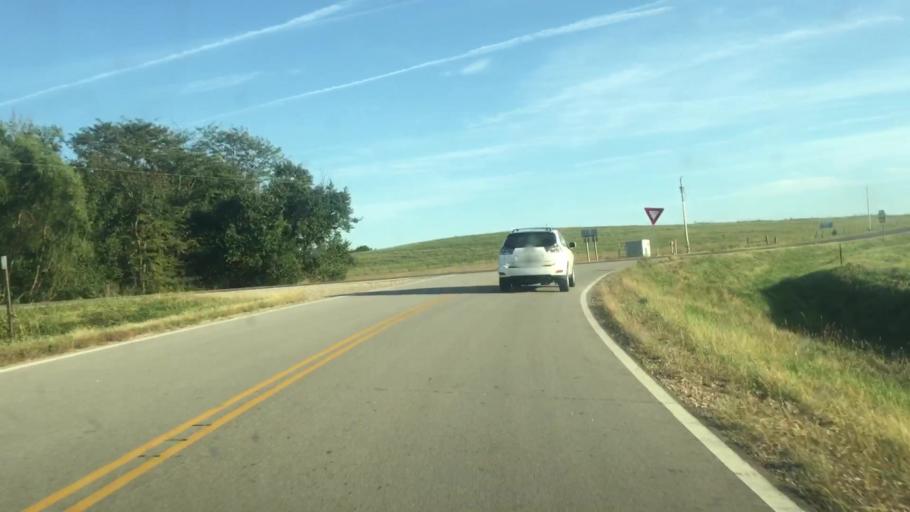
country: US
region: Kansas
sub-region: Brown County
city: Horton
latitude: 39.5867
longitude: -95.5272
